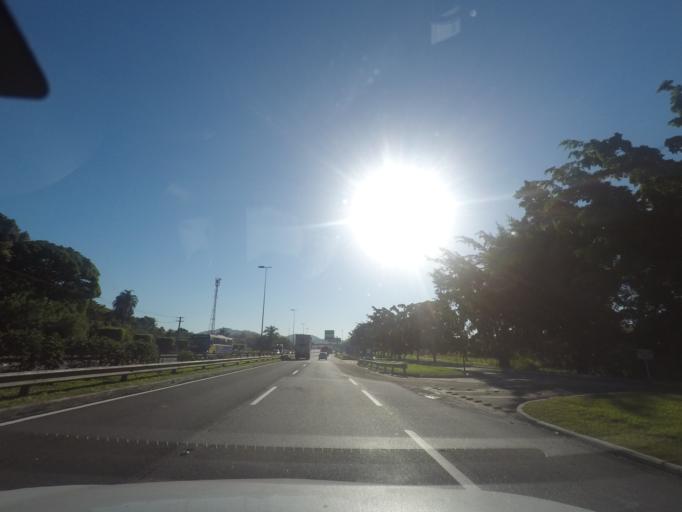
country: BR
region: Rio de Janeiro
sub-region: Petropolis
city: Petropolis
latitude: -22.6469
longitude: -43.1928
